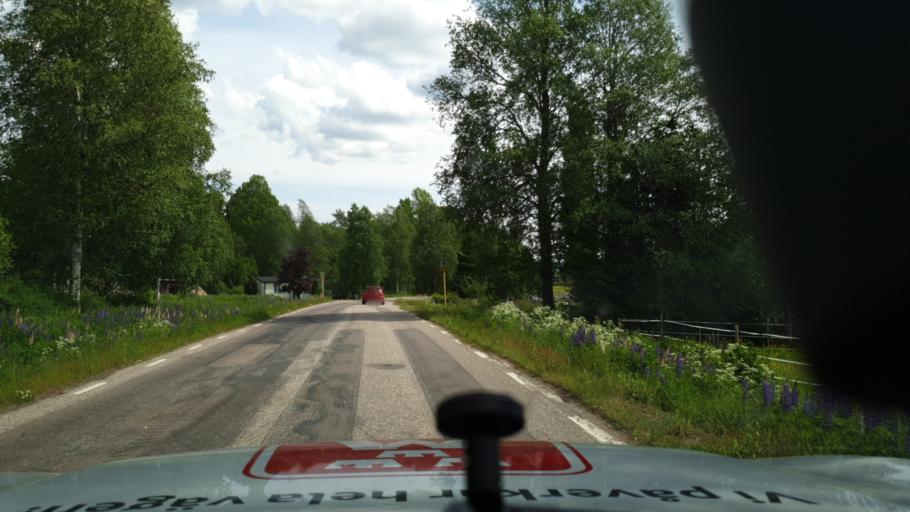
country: SE
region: Vaermland
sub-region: Torsby Kommun
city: Torsby
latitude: 59.9879
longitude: 12.8577
